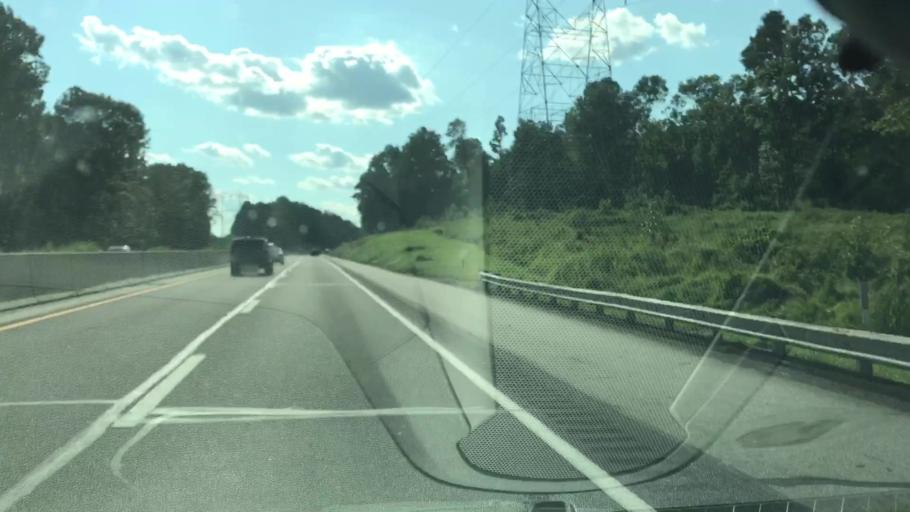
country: US
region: Pennsylvania
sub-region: Lebanon County
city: Cornwall
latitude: 40.2272
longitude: -76.4716
